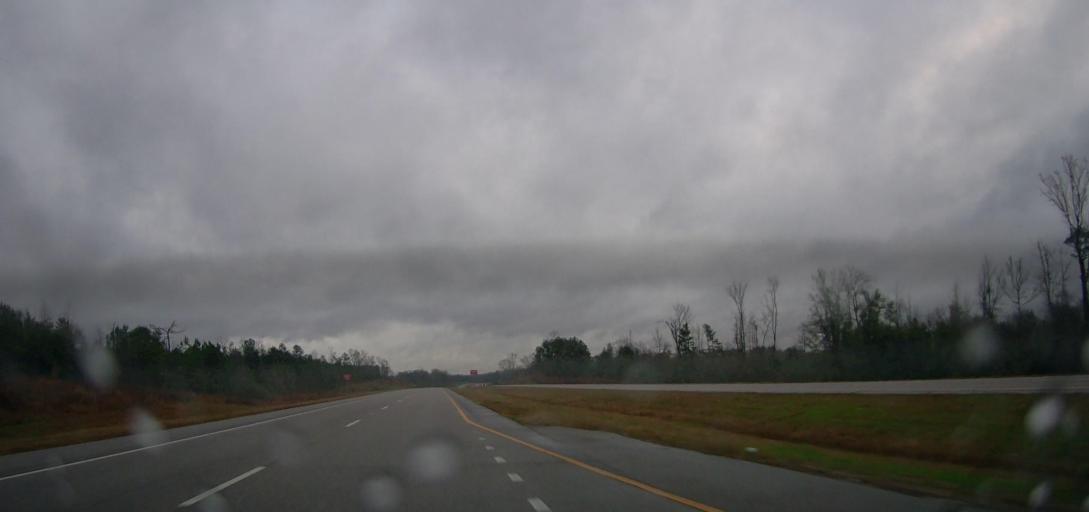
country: US
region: Alabama
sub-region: Bibb County
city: Centreville
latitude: 32.9433
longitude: -87.0818
